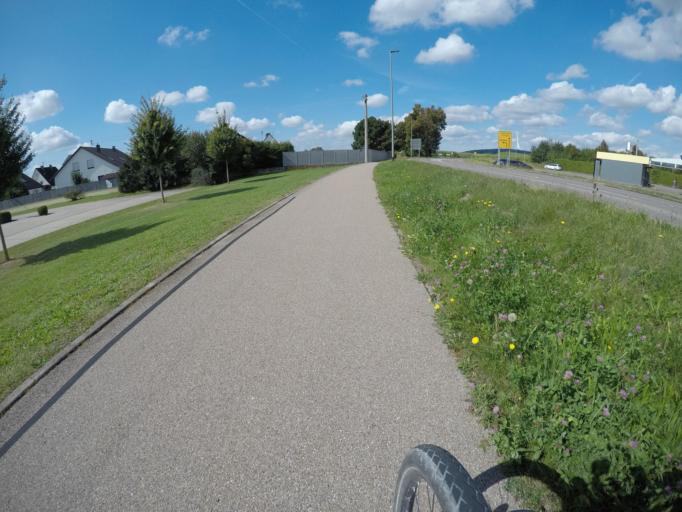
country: DE
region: Bavaria
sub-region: Swabia
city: Hochstadt an der Donau
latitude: 48.6205
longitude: 10.5601
